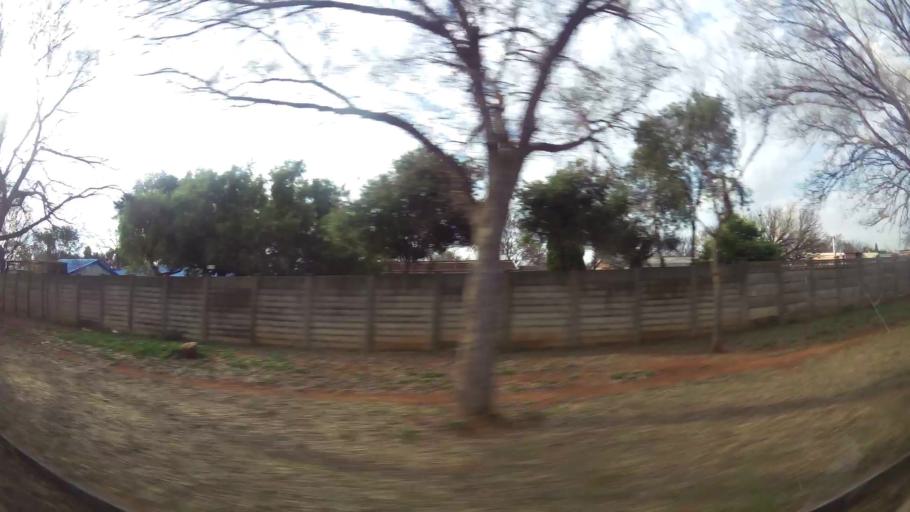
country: ZA
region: Orange Free State
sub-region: Fezile Dabi District Municipality
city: Sasolburg
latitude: -26.8182
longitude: 27.8130
